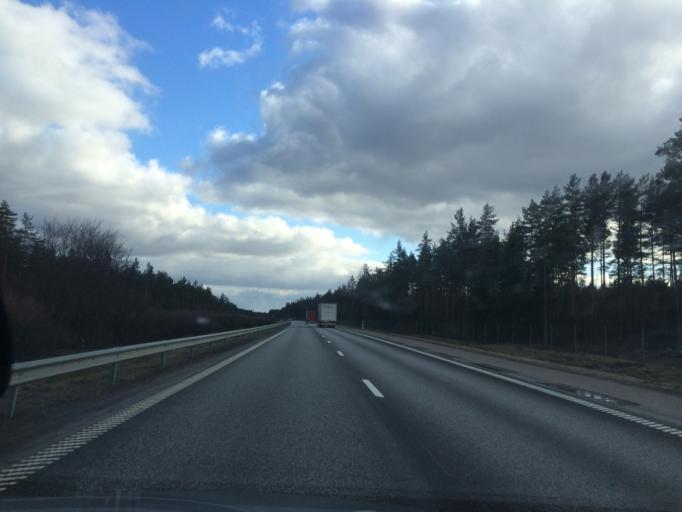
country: SE
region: Joenkoeping
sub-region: Vaggeryds Kommun
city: Skillingaryd
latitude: 57.3777
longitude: 14.1005
